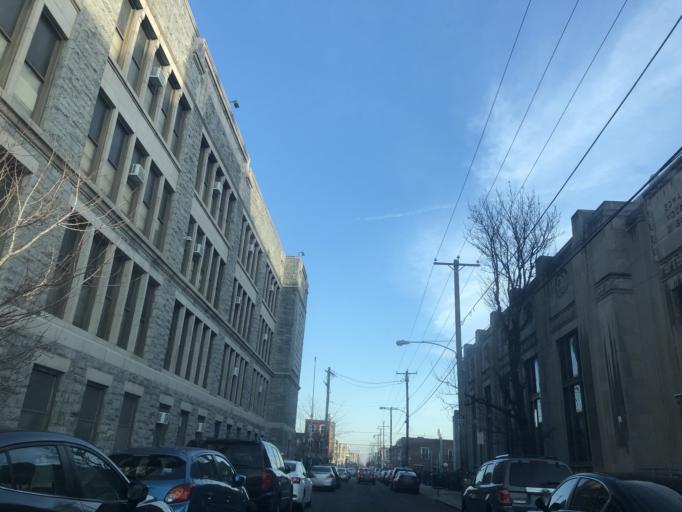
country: US
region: Pennsylvania
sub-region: Philadelphia County
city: Philadelphia
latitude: 39.9257
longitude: -75.1605
